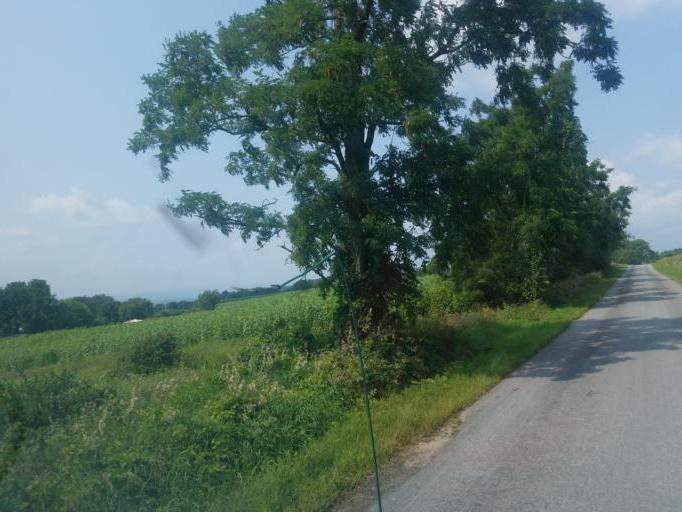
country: US
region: New York
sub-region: Montgomery County
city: Wellsville
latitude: 42.8683
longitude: -74.3273
